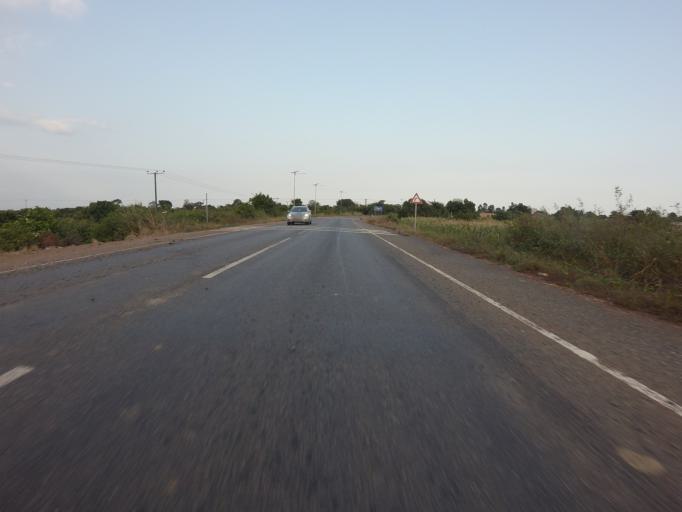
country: GH
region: Volta
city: Anloga
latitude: 6.0758
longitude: 0.6027
